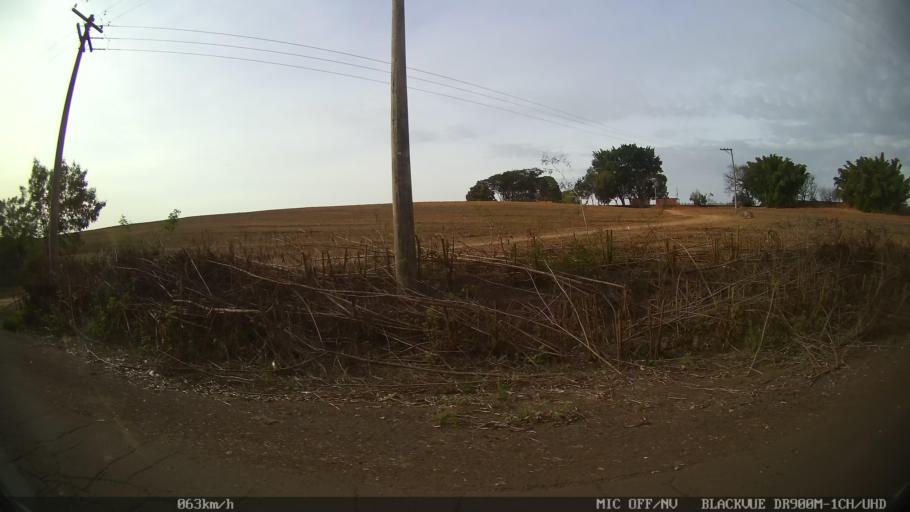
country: BR
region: Sao Paulo
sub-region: Piracicaba
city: Piracicaba
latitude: -22.7044
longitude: -47.5860
